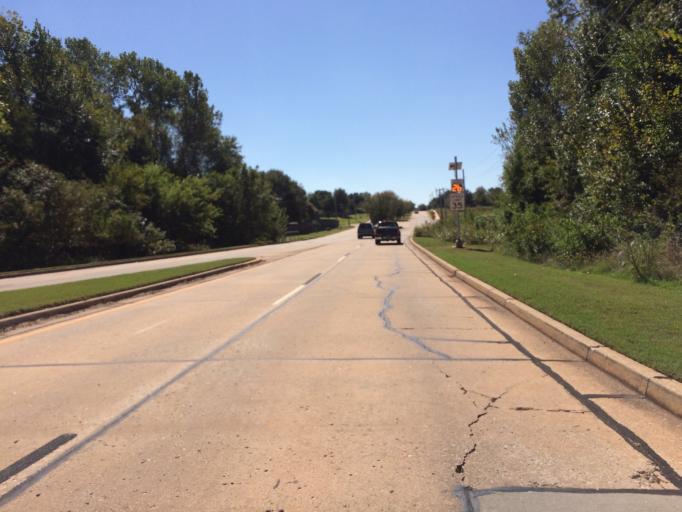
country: US
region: Oklahoma
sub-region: Cleveland County
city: Hall Park
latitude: 35.2466
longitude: -97.4062
